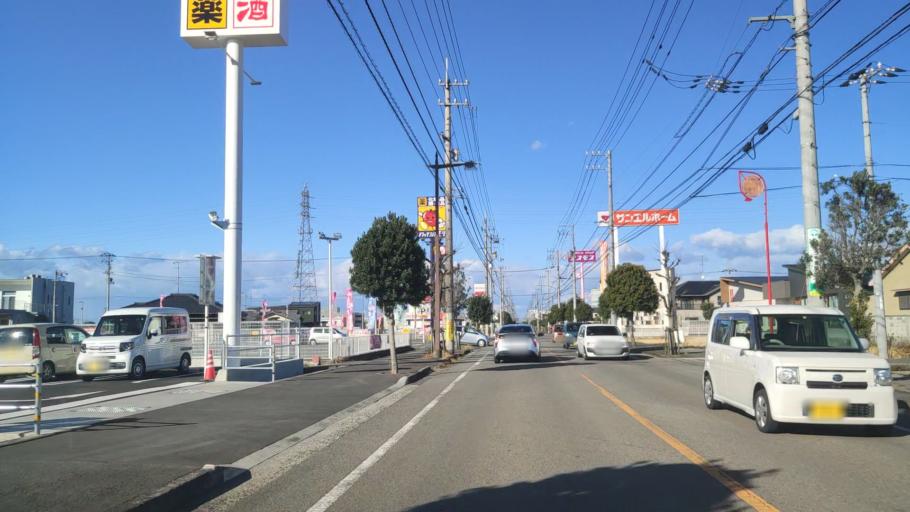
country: JP
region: Ehime
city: Saijo
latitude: 33.9245
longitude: 133.1911
